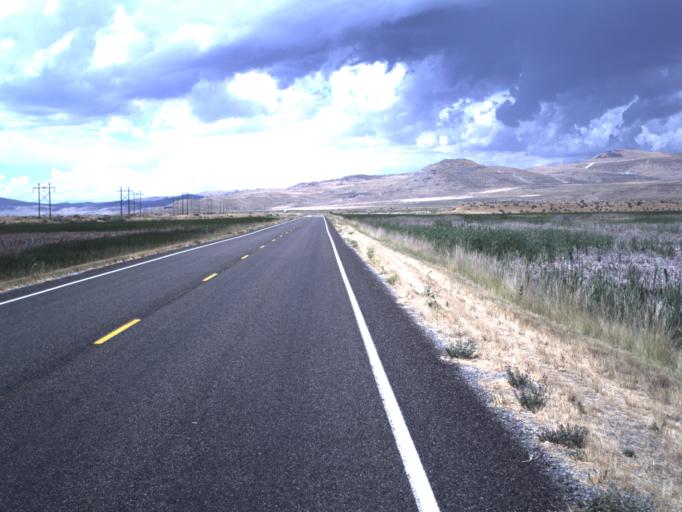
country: US
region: Utah
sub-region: Box Elder County
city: Tremonton
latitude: 41.6060
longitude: -112.3208
